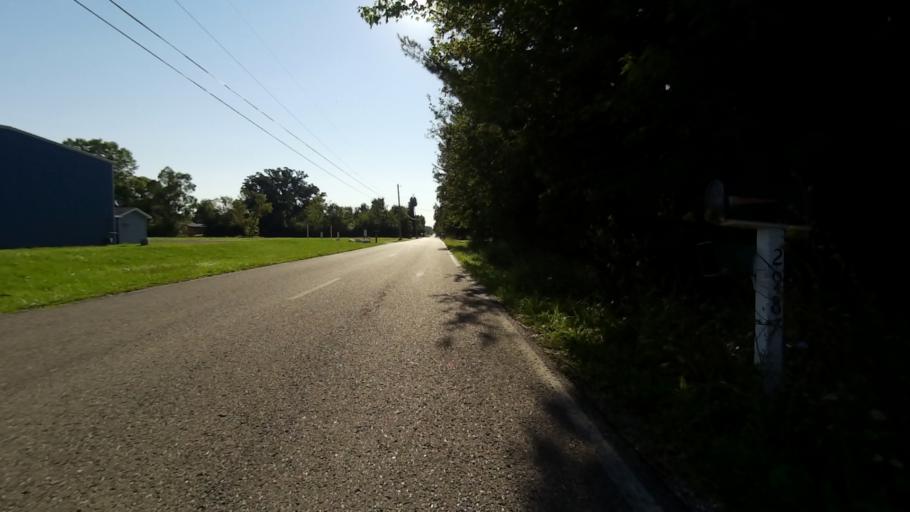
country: US
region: Ohio
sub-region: Portage County
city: Mantua
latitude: 41.2968
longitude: -81.2852
